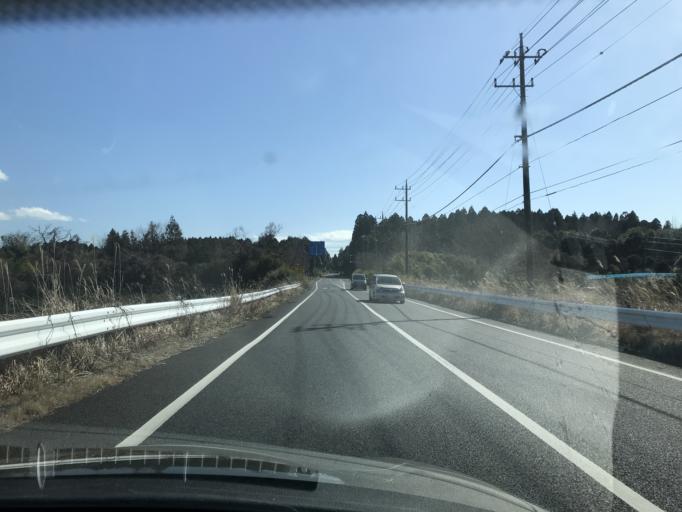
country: JP
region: Chiba
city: Sawara
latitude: 35.8187
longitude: 140.5192
